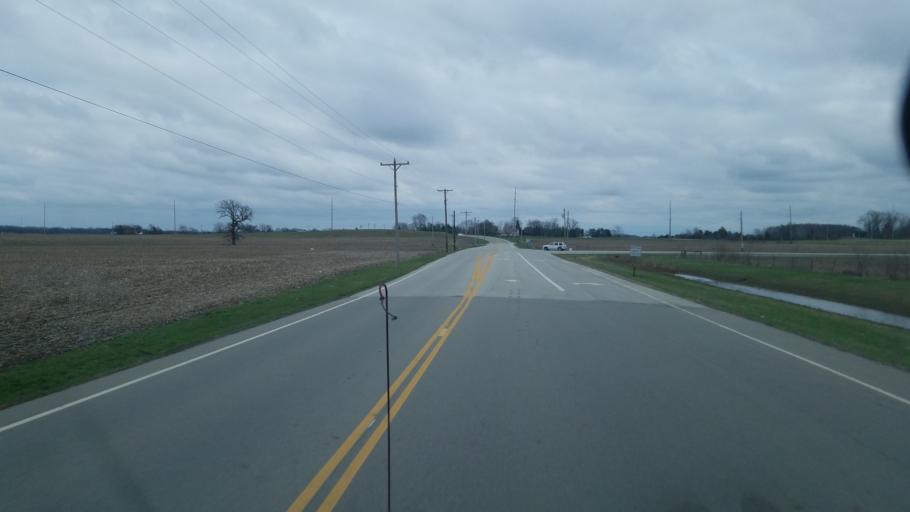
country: US
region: Ohio
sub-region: Fayette County
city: Washington Court House
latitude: 39.5521
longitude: -83.4869
